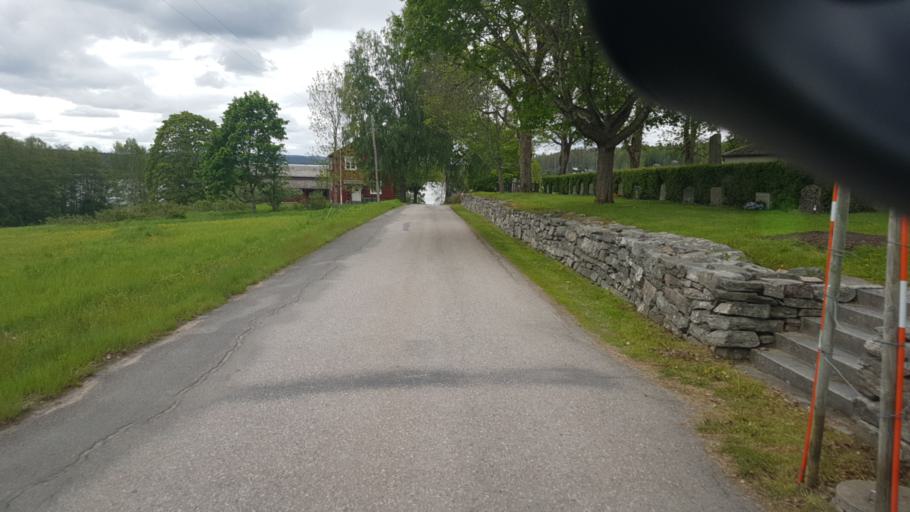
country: SE
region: Vaermland
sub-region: Arvika Kommun
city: Arvika
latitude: 59.8123
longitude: 12.5656
